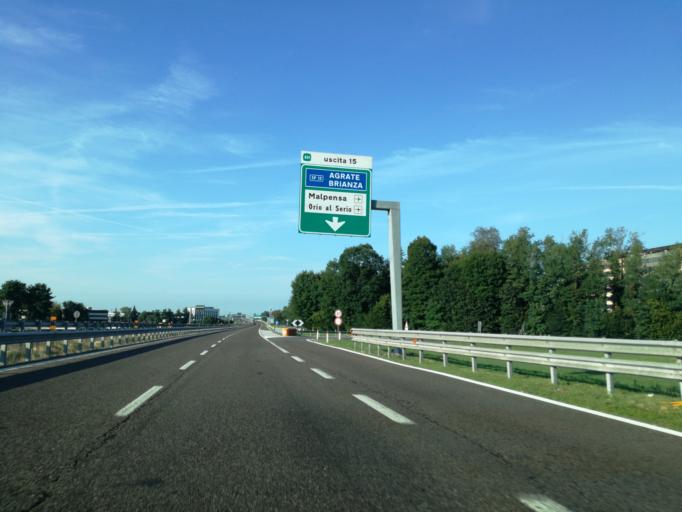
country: IT
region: Lombardy
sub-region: Provincia di Monza e Brianza
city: Agrate Brianza
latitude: 45.5743
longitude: 9.3406
